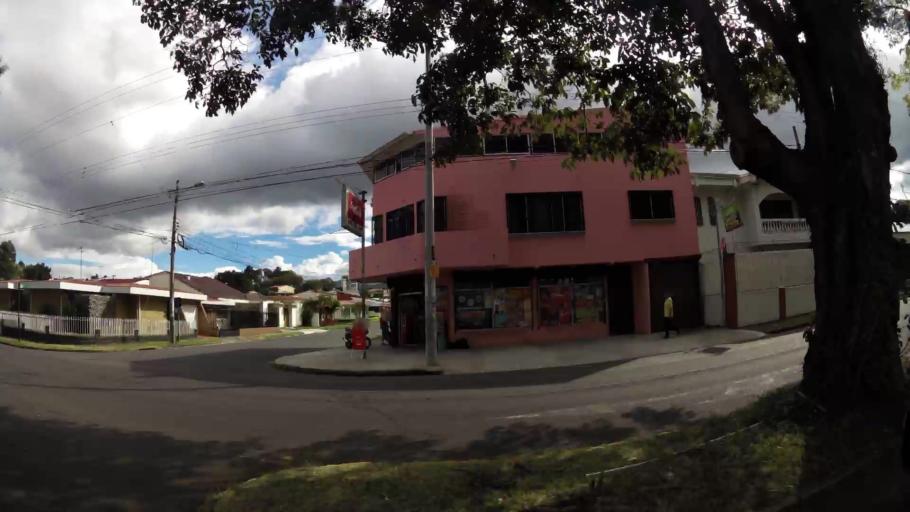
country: CR
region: San Jose
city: San Rafael
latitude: 9.9472
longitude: -84.1274
